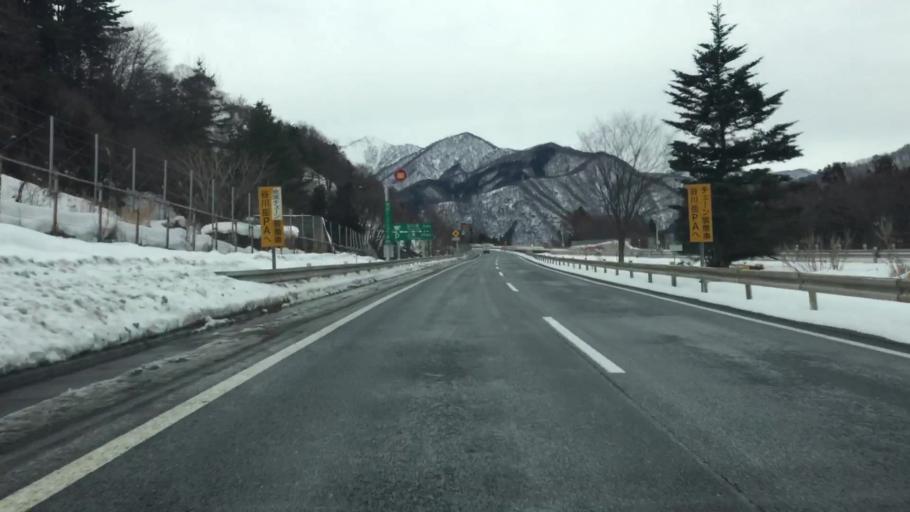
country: JP
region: Gunma
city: Numata
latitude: 36.7578
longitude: 138.9660
